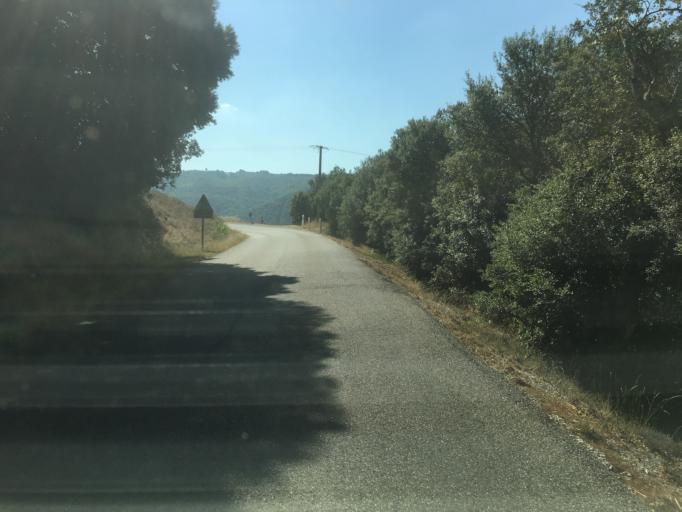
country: FR
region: Provence-Alpes-Cote d'Azur
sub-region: Departement des Alpes-de-Haute-Provence
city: Oraison
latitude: 43.8910
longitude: 5.9567
